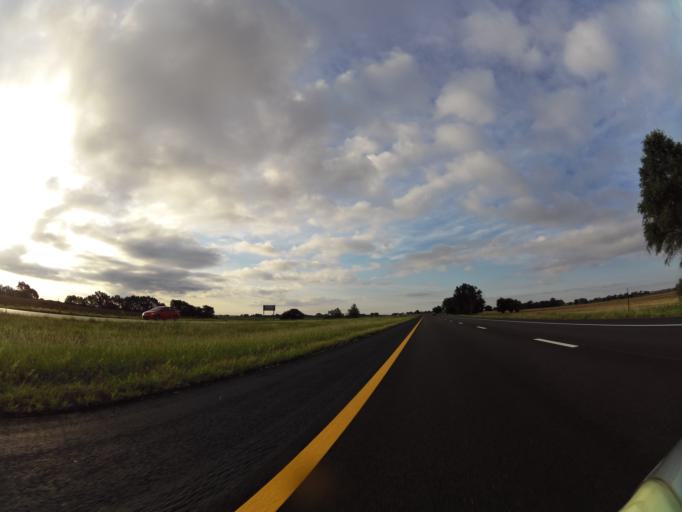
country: US
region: Kansas
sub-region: Sedgwick County
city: Colwich
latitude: 37.8671
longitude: -97.6224
